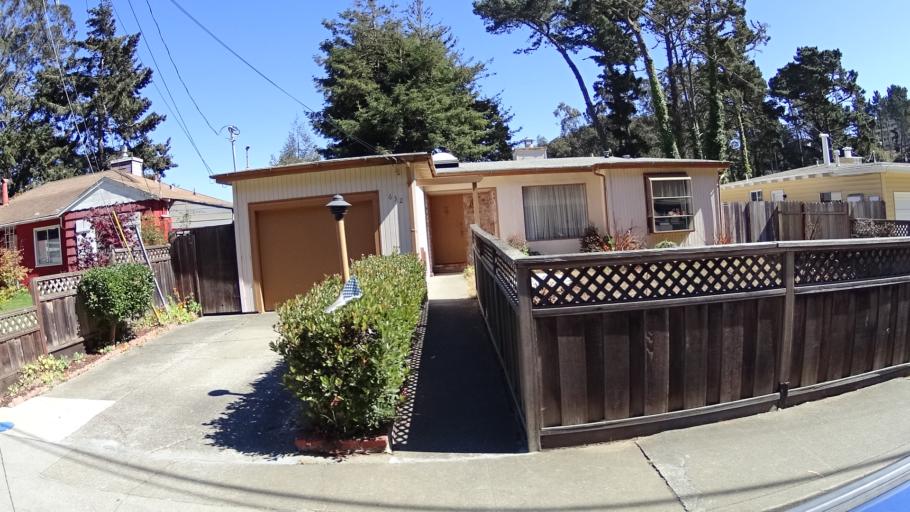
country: US
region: California
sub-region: San Mateo County
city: Broadmoor
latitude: 37.6881
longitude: -122.4836
